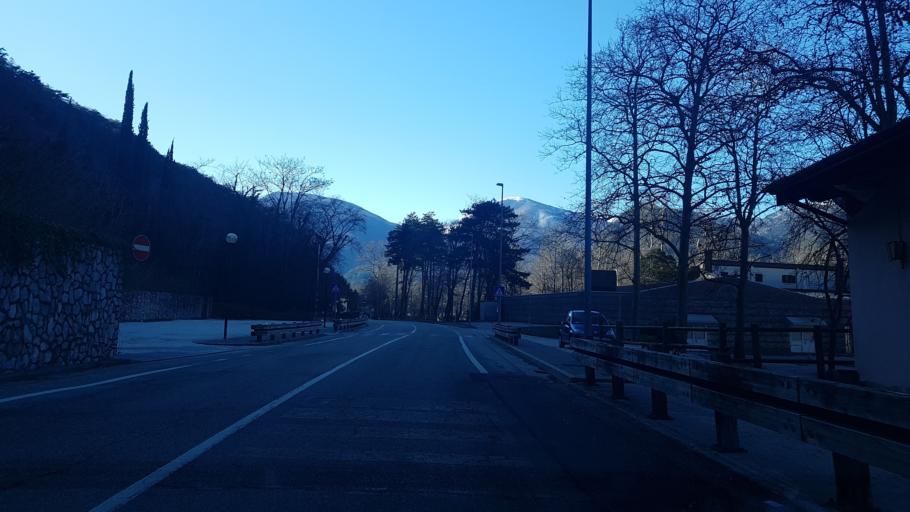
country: IT
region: Friuli Venezia Giulia
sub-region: Provincia di Udine
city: Bordano
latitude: 46.3205
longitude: 13.0704
